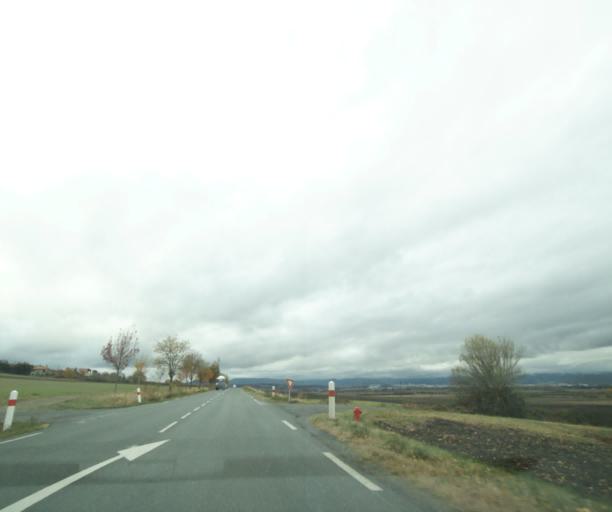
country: FR
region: Auvergne
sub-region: Departement du Puy-de-Dome
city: Pont-du-Chateau
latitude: 45.8091
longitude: 3.2324
